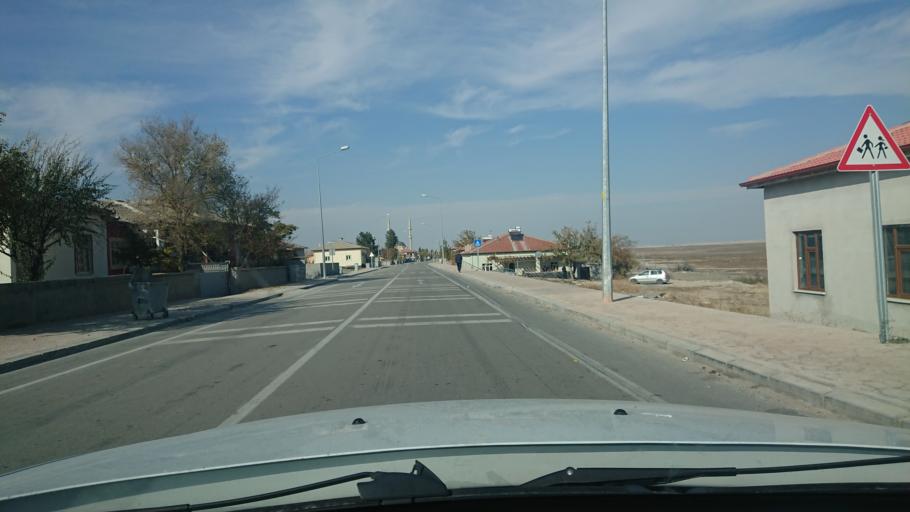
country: TR
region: Aksaray
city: Sultanhani
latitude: 38.2544
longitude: 33.4480
